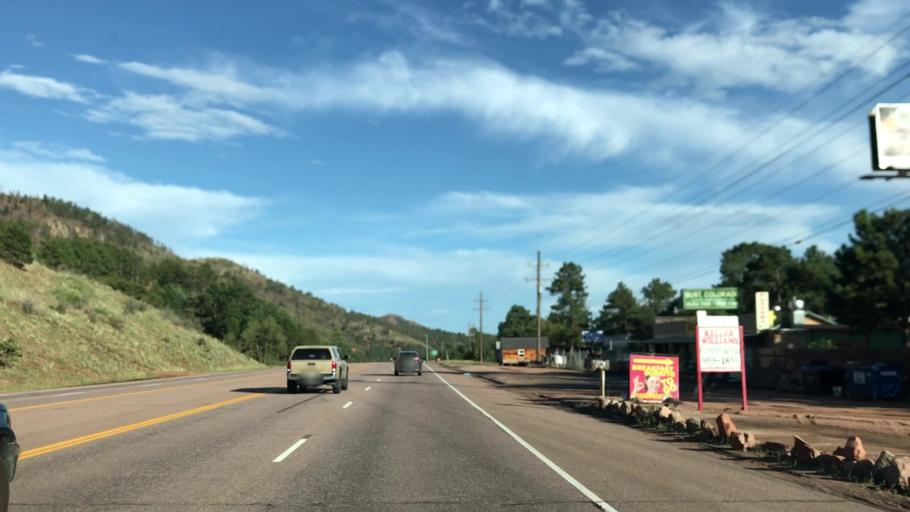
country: US
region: Colorado
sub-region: El Paso County
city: Cascade-Chipita Park
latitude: 38.9153
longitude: -104.9808
